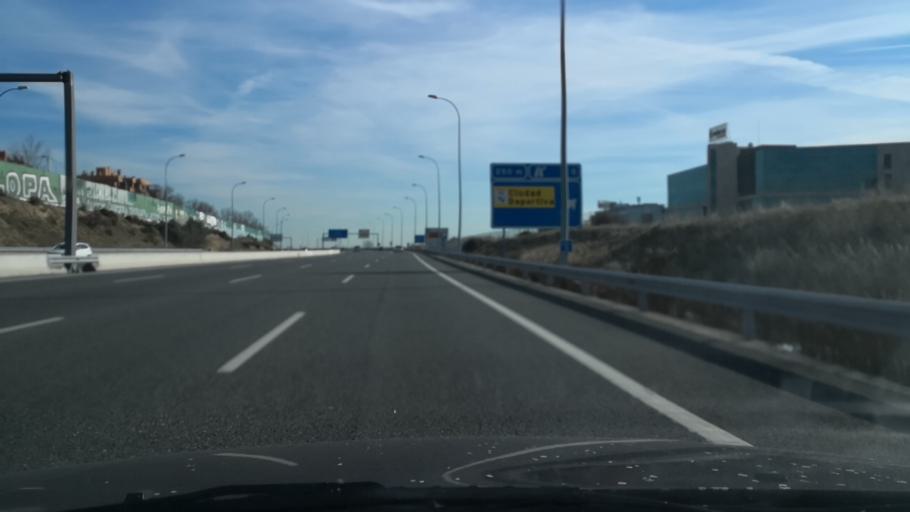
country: ES
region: Madrid
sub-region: Provincia de Madrid
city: Hortaleza
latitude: 40.4767
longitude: -3.6321
